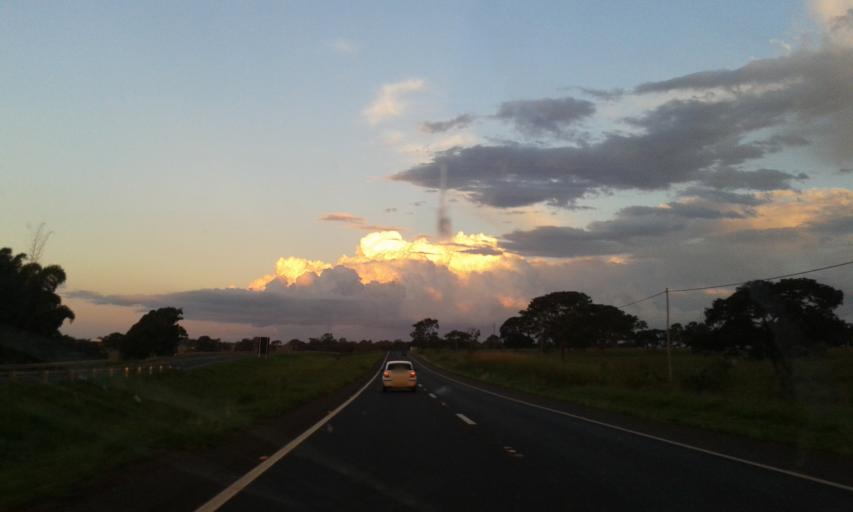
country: BR
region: Minas Gerais
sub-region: Monte Alegre De Minas
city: Monte Alegre de Minas
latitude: -18.8920
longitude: -48.6660
